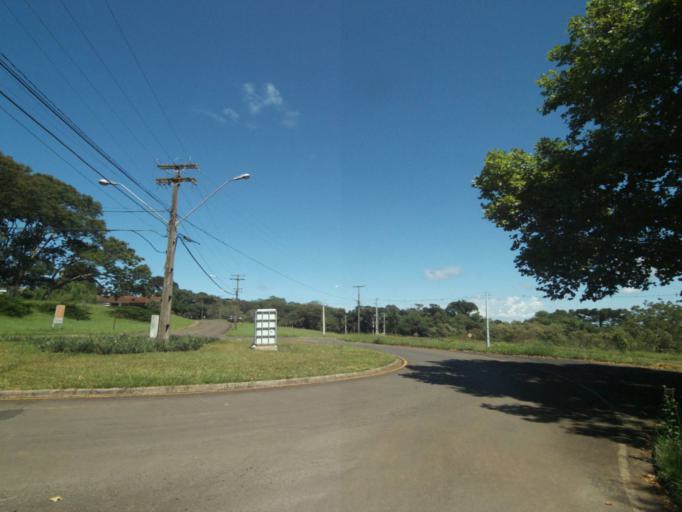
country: BR
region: Parana
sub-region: Pinhao
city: Pinhao
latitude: -25.7922
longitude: -52.0873
